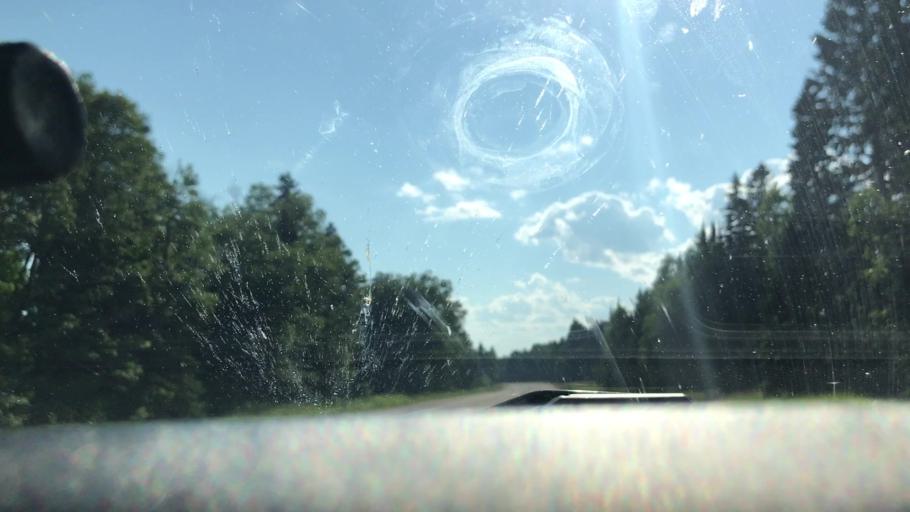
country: US
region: Minnesota
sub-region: Cook County
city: Grand Marais
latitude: 47.8124
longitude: -90.0660
